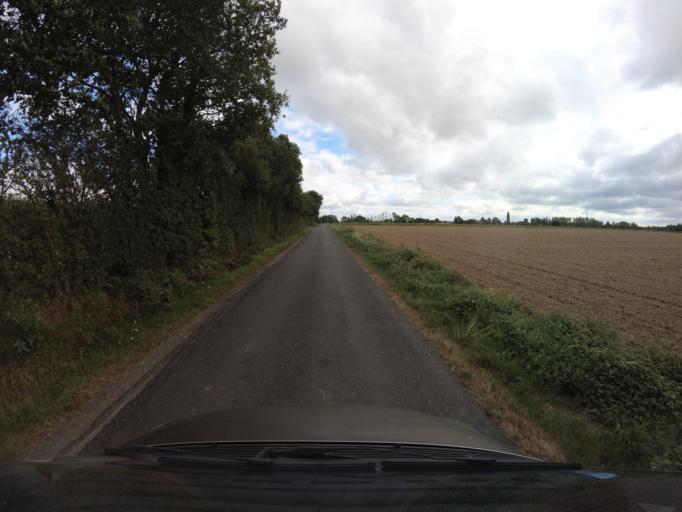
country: FR
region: Pays de la Loire
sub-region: Departement de la Vendee
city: Saint-Philbert-de-Bouaine
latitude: 46.9991
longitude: -1.5261
